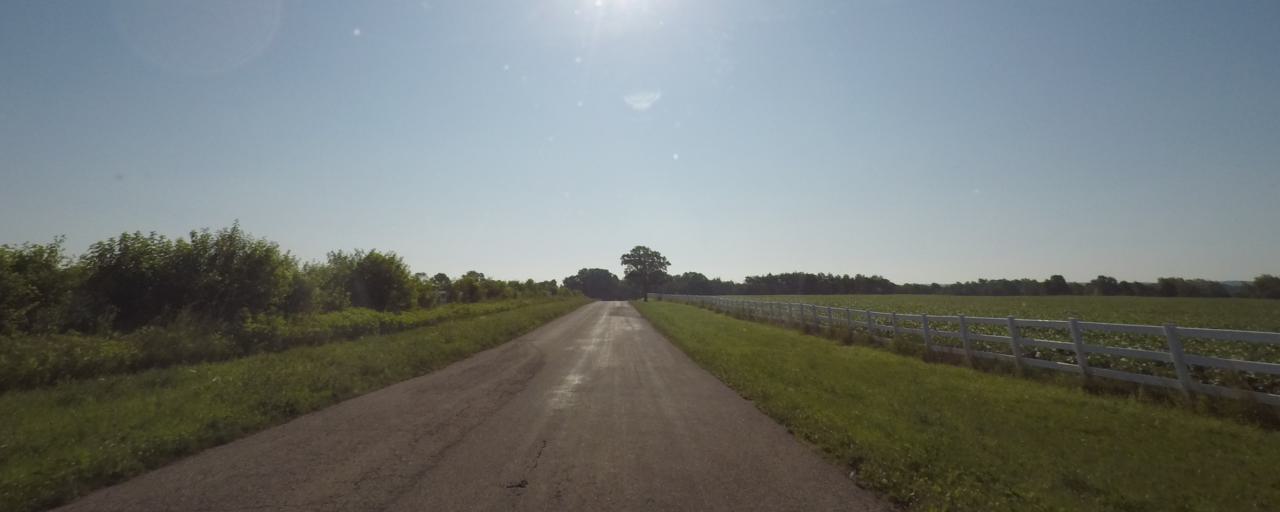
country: US
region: Wisconsin
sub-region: Jefferson County
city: Palmyra
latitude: 42.9190
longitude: -88.5519
